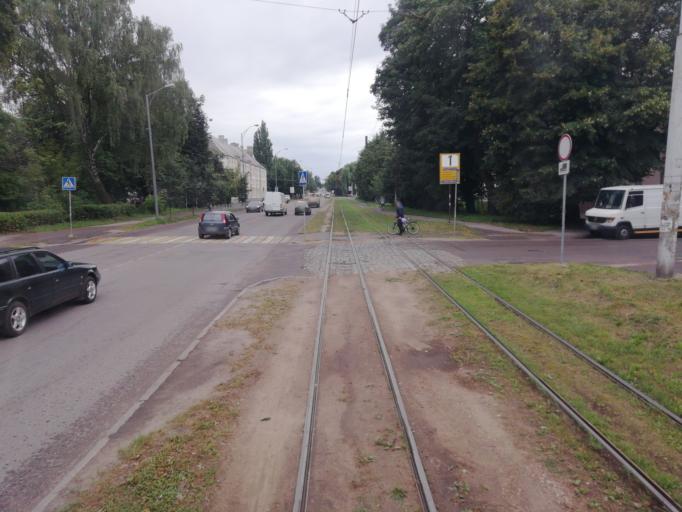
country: RU
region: Kaliningrad
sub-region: Gorod Kaliningrad
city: Kaliningrad
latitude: 54.6878
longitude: 20.5230
